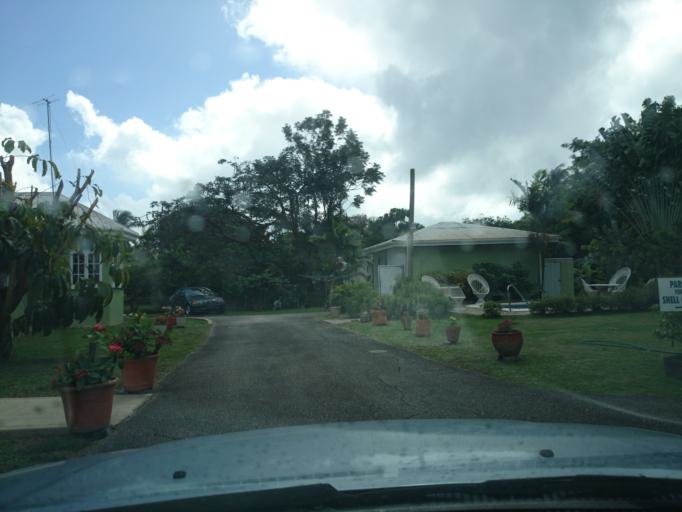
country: BB
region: Saint Peter
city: Speightstown
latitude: 13.2281
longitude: -59.6407
